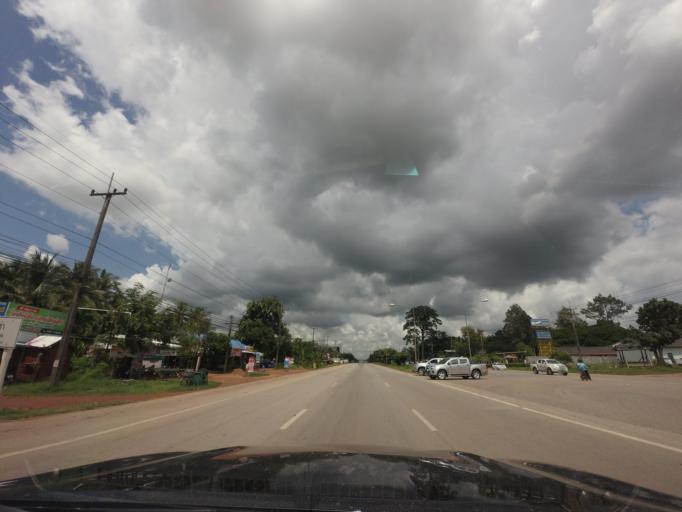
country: TH
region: Changwat Udon Thani
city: Udon Thani
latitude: 17.5451
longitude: 102.8005
